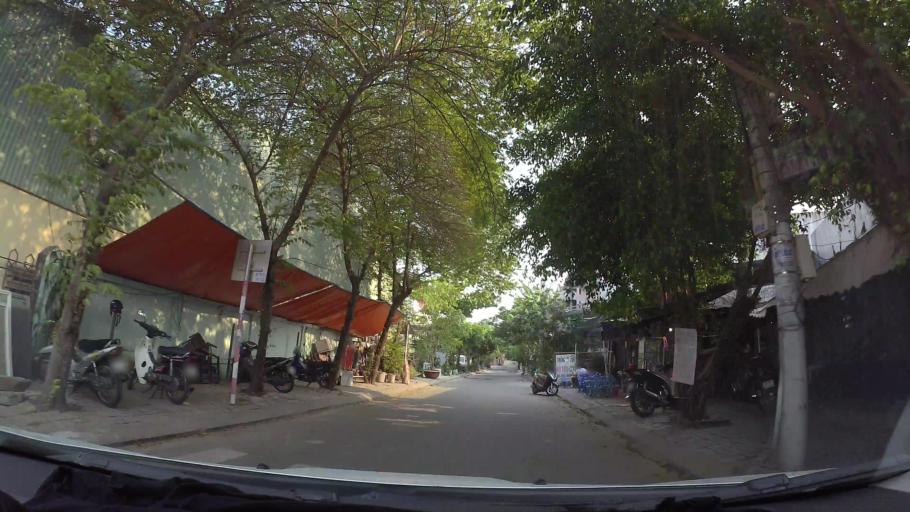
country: VN
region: Da Nang
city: Cam Le
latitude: 16.0210
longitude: 108.2060
